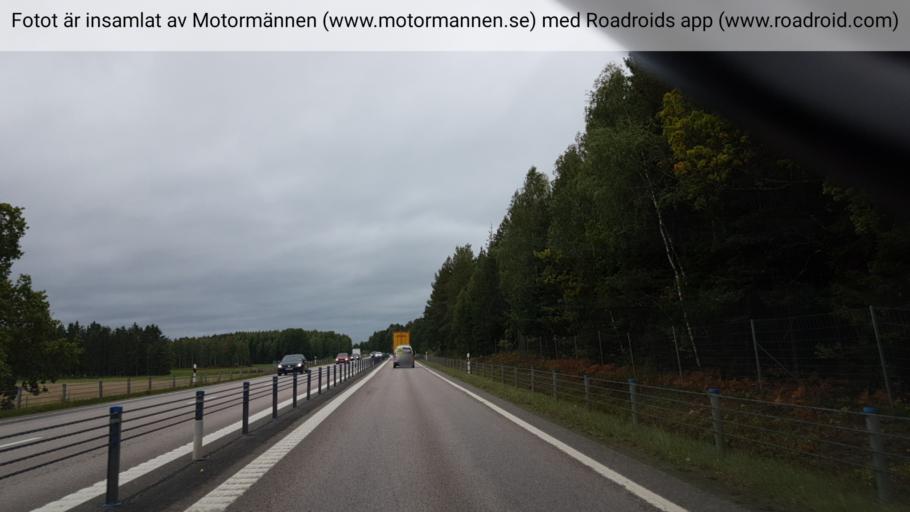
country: SE
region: Vaestra Goetaland
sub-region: Skovde Kommun
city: Stopen
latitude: 58.5416
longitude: 13.8119
